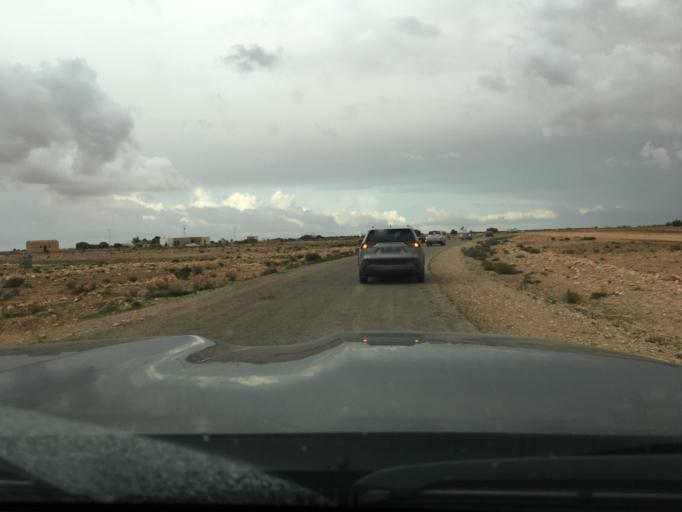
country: TN
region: Madanin
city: Medenine
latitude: 33.3032
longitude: 10.6110
